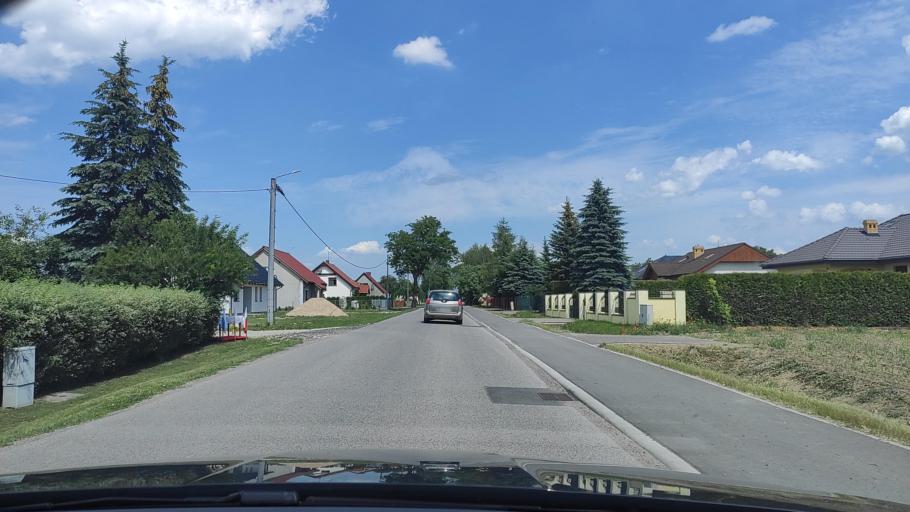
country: PL
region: Greater Poland Voivodeship
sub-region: Powiat gnieznienski
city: Lubowo
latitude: 52.5164
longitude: 17.3862
